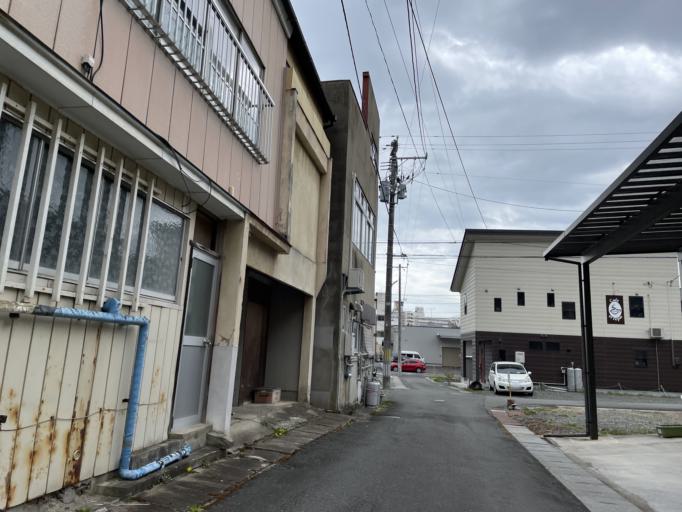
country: JP
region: Iwate
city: Ofunato
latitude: 38.9083
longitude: 141.5758
